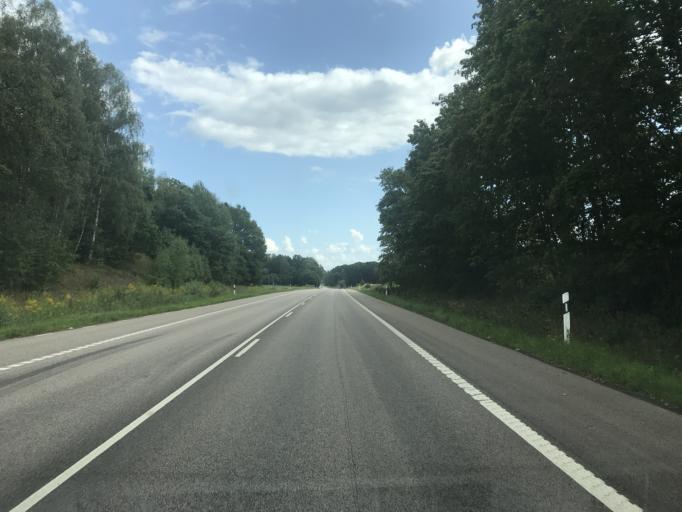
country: SE
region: Skane
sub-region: Hassleholms Kommun
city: Hassleholm
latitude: 56.1393
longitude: 13.8044
